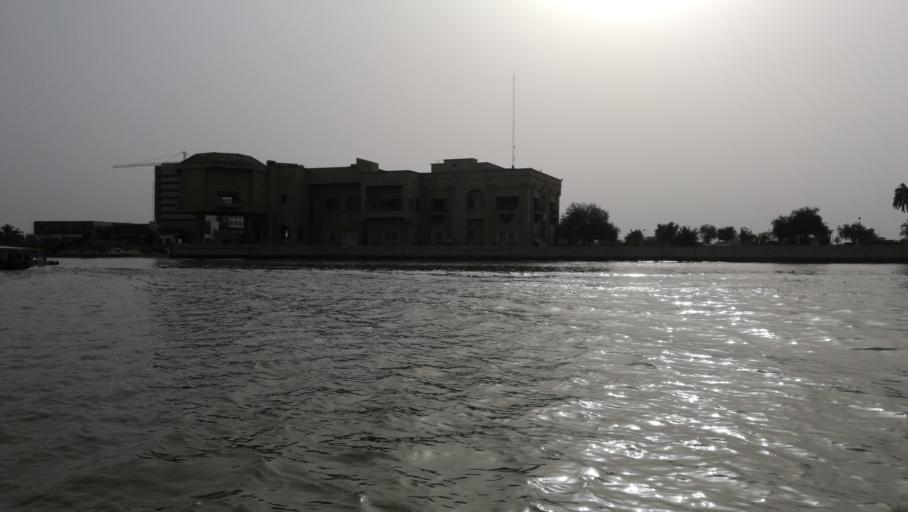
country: IQ
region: Basra Governorate
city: Al Basrah al Qadimah
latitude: 30.4969
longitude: 47.8649
